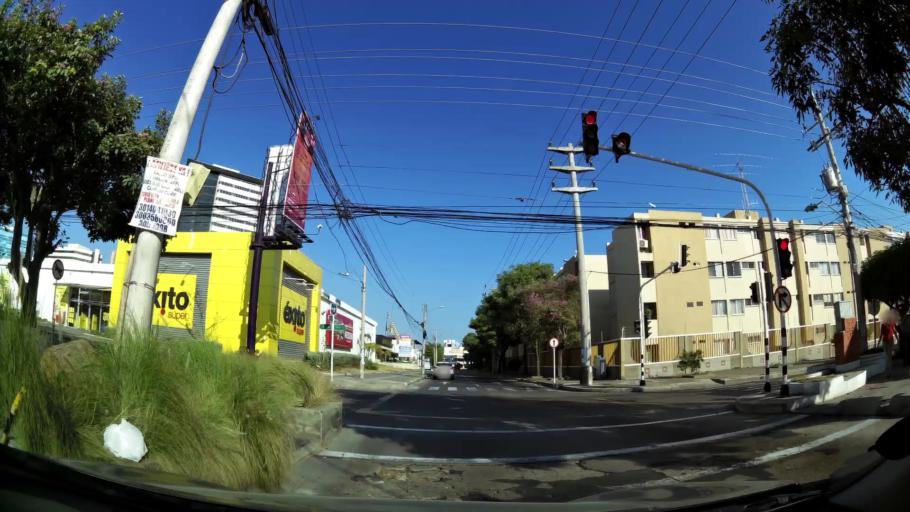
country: CO
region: Atlantico
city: Barranquilla
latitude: 11.0067
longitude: -74.8001
